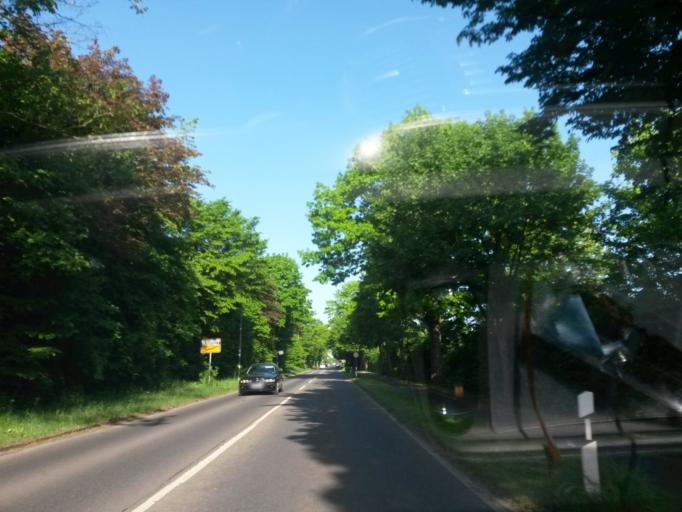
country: DE
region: North Rhine-Westphalia
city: Sankt Augustin
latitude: 50.7708
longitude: 7.2005
